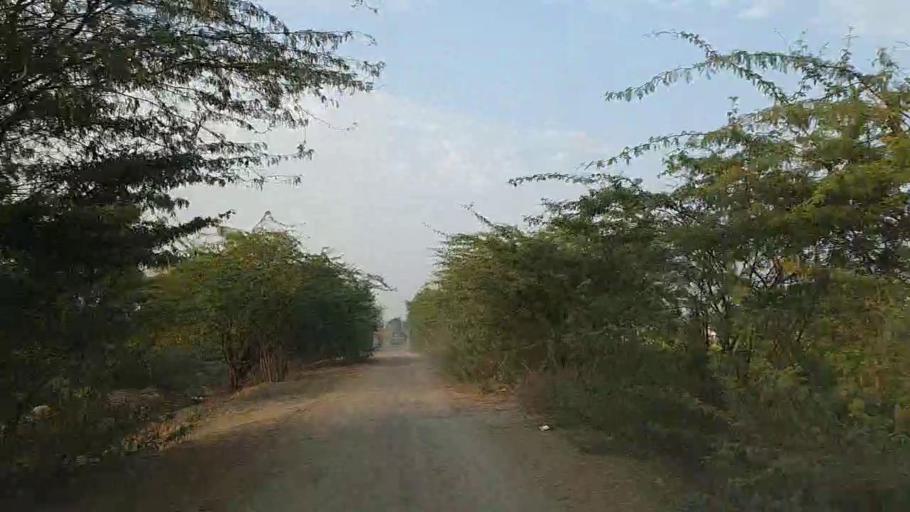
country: PK
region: Sindh
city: Jam Sahib
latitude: 26.3171
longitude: 68.6090
